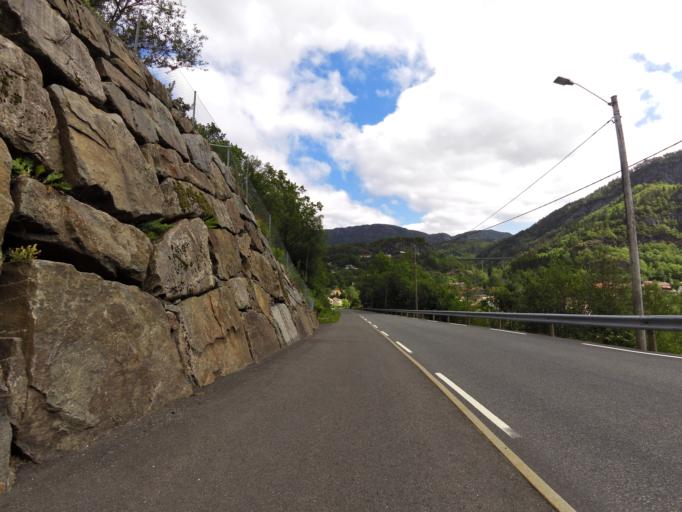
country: NO
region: Vest-Agder
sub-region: Flekkefjord
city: Flekkefjord
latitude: 58.2693
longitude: 6.8098
